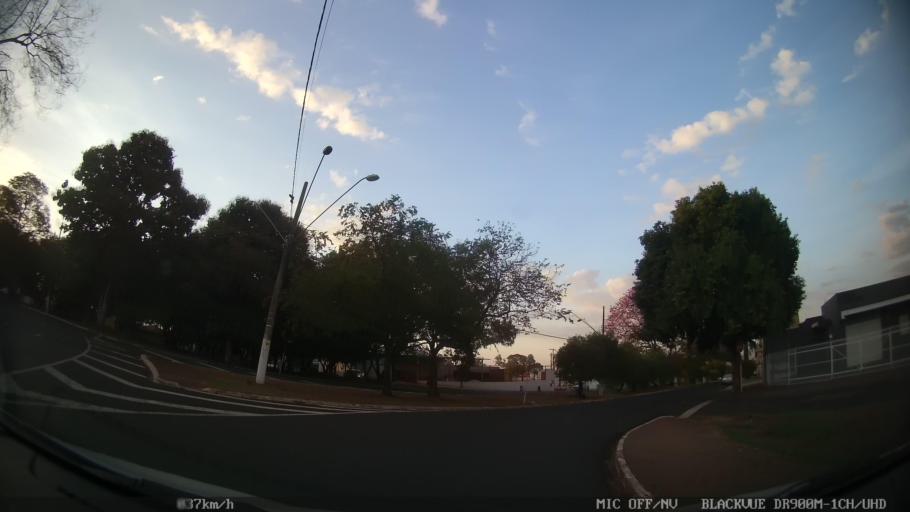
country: BR
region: Sao Paulo
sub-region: Ribeirao Preto
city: Ribeirao Preto
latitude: -21.1356
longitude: -47.8461
